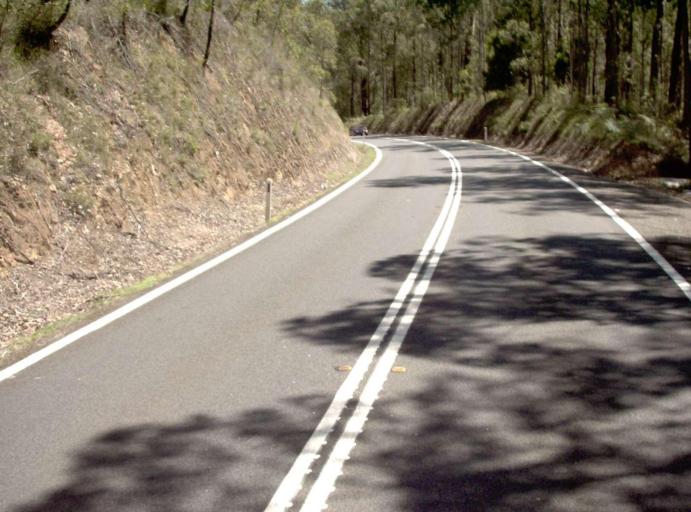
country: AU
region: New South Wales
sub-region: Bombala
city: Bombala
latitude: -37.5832
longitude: 148.9203
